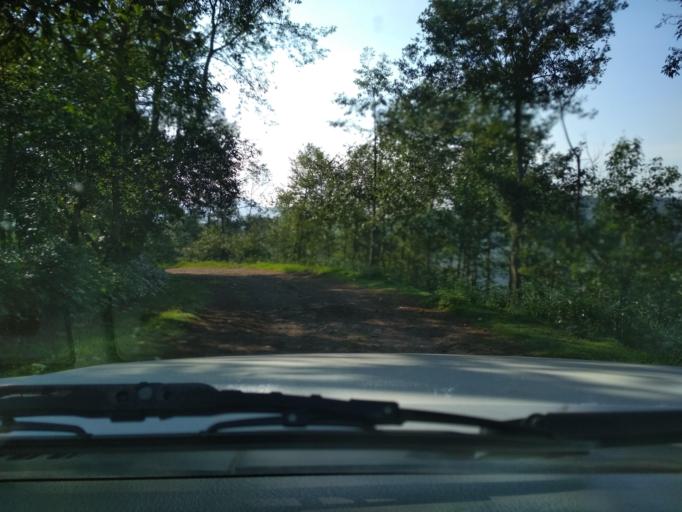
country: MX
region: Veracruz
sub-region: La Perla
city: Chilapa
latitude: 18.9855
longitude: -97.1672
